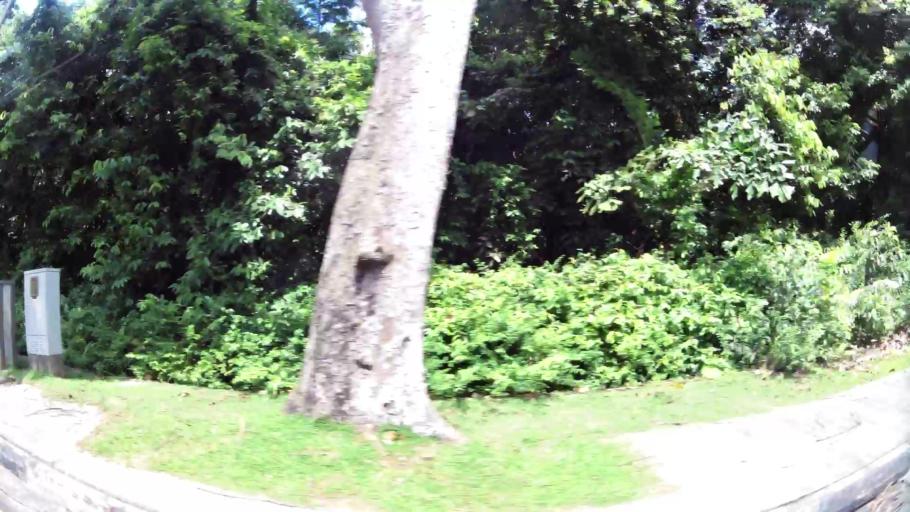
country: SG
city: Singapore
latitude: 1.3383
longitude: 103.8035
